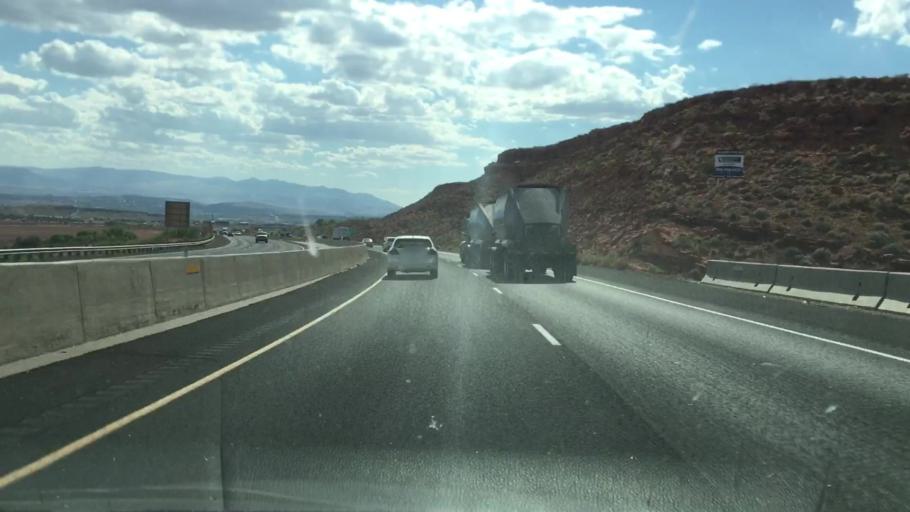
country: US
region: Utah
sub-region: Washington County
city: Washington
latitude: 37.1587
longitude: -113.4751
